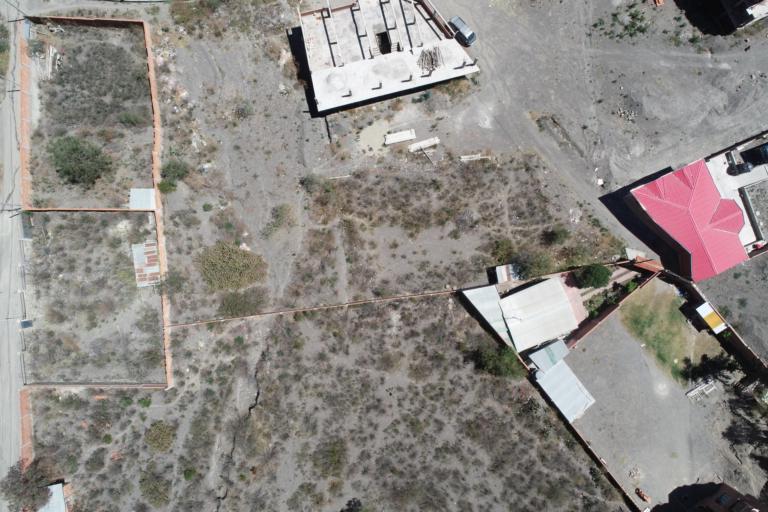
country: BO
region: La Paz
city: La Paz
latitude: -16.6280
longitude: -68.0510
